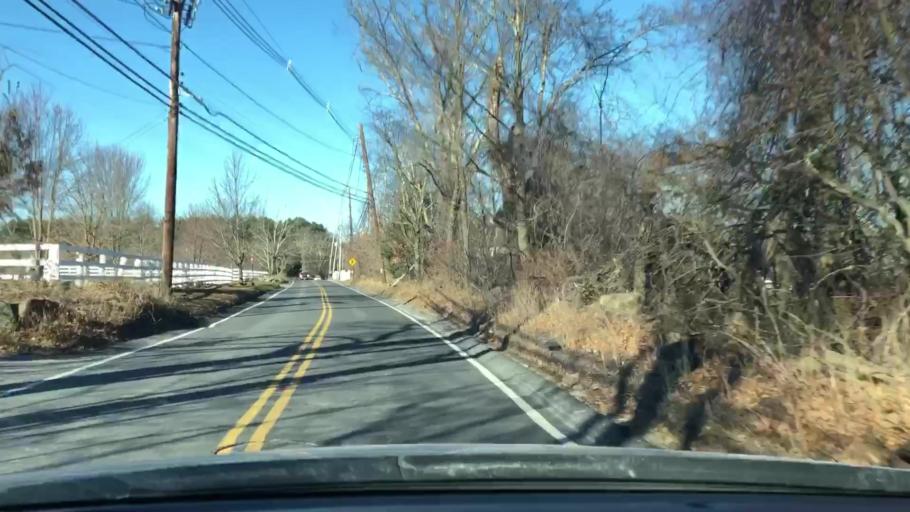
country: US
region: Massachusetts
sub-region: Norfolk County
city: Westwood
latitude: 42.1845
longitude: -71.2461
